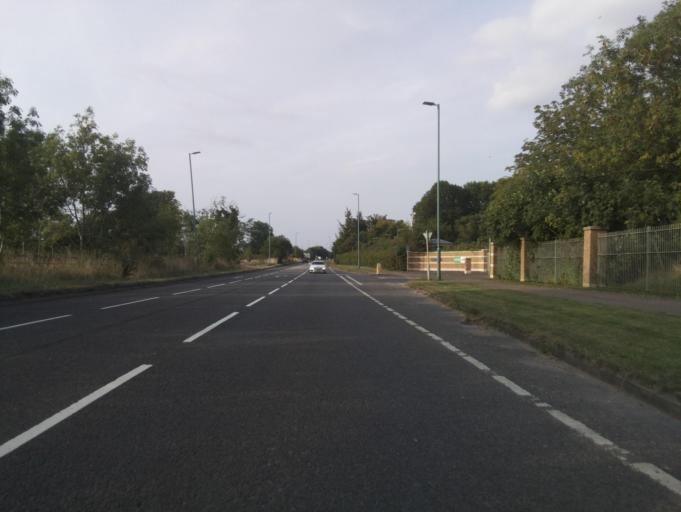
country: GB
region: England
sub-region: Gloucestershire
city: Gotherington
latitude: 51.9427
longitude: -2.0724
